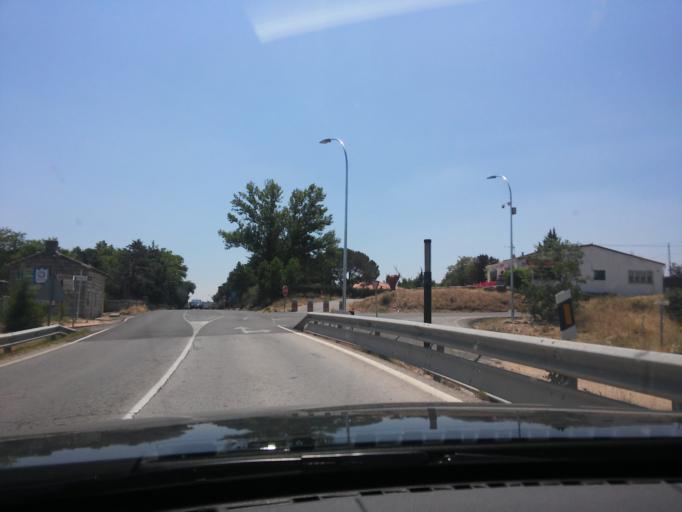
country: ES
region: Madrid
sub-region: Provincia de Madrid
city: Collado-Villalba
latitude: 40.6279
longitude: -4.0297
